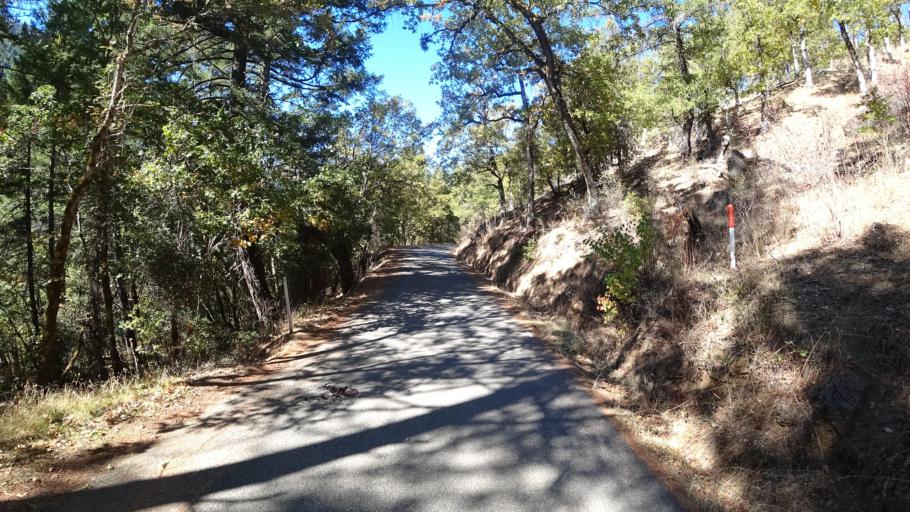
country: US
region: California
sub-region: Humboldt County
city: Willow Creek
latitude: 41.2805
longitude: -123.3496
